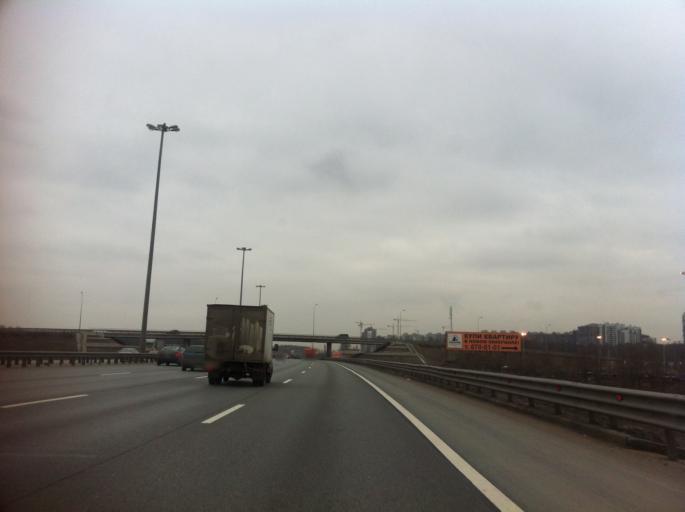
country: RU
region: St.-Petersburg
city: Krasnogvargeisky
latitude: 59.9179
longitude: 30.5256
